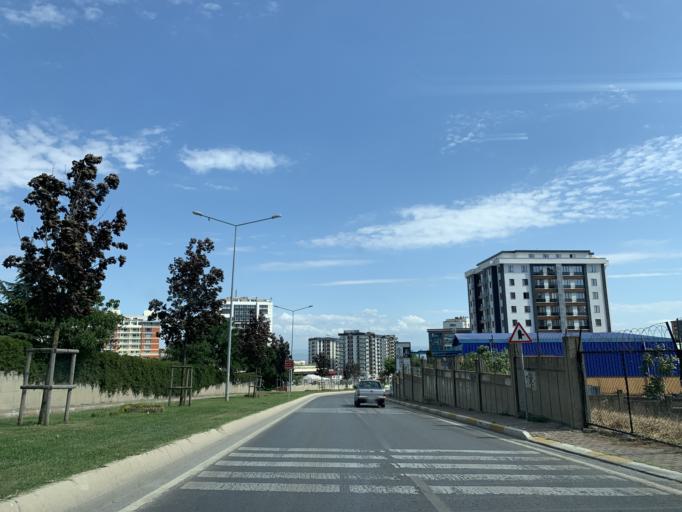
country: TR
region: Istanbul
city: Pendik
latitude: 40.8937
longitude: 29.2620
